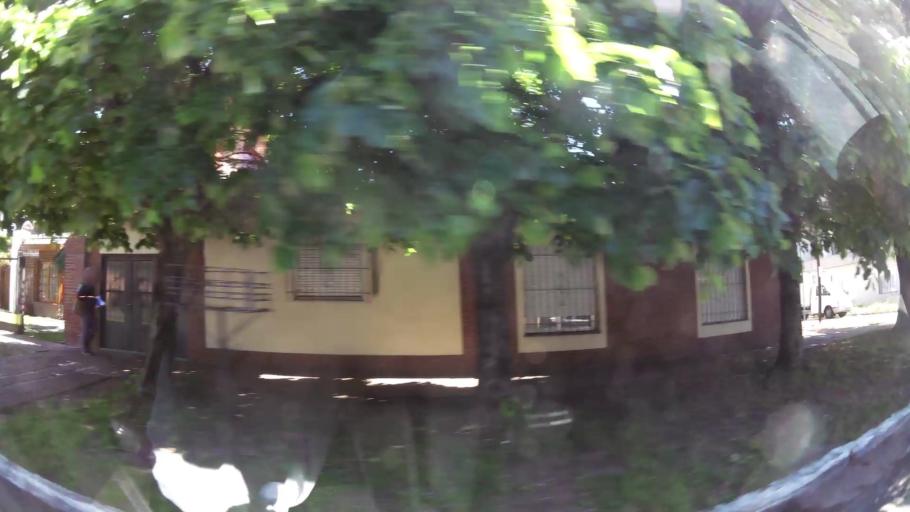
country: AR
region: Buenos Aires
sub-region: Partido de Quilmes
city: Quilmes
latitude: -34.7238
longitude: -58.2801
